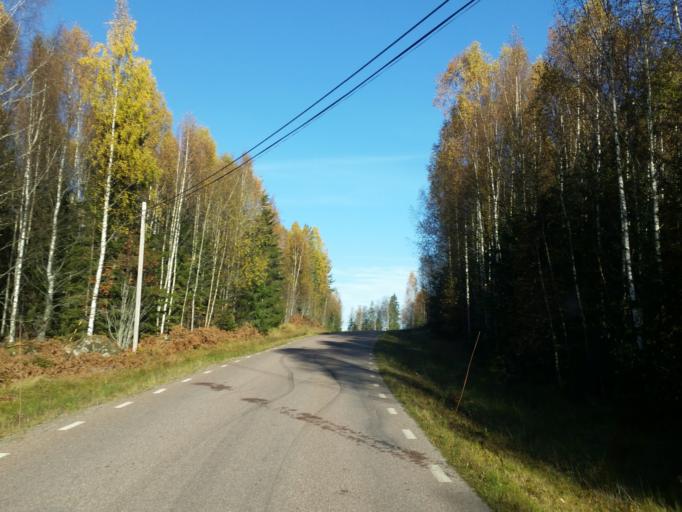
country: SE
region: Dalarna
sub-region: Borlange Kommun
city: Ornas
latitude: 60.4536
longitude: 15.6169
